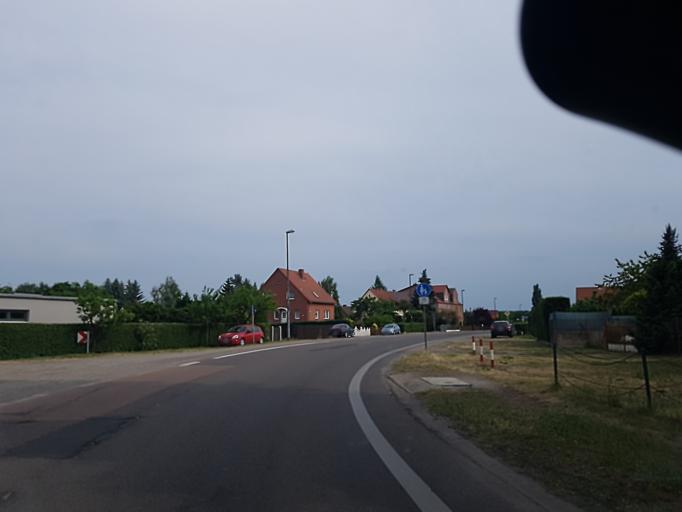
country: DE
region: Saxony-Anhalt
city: Wittenburg
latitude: 51.8681
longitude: 12.6765
